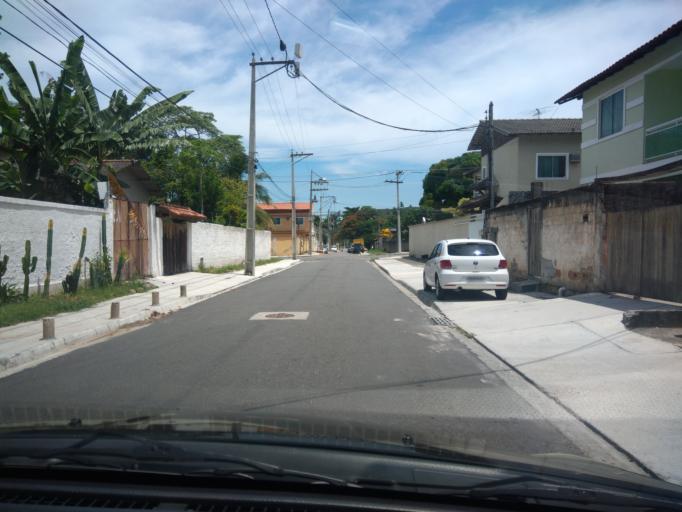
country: BR
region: Rio de Janeiro
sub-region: Niteroi
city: Niteroi
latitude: -22.9289
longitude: -43.0709
